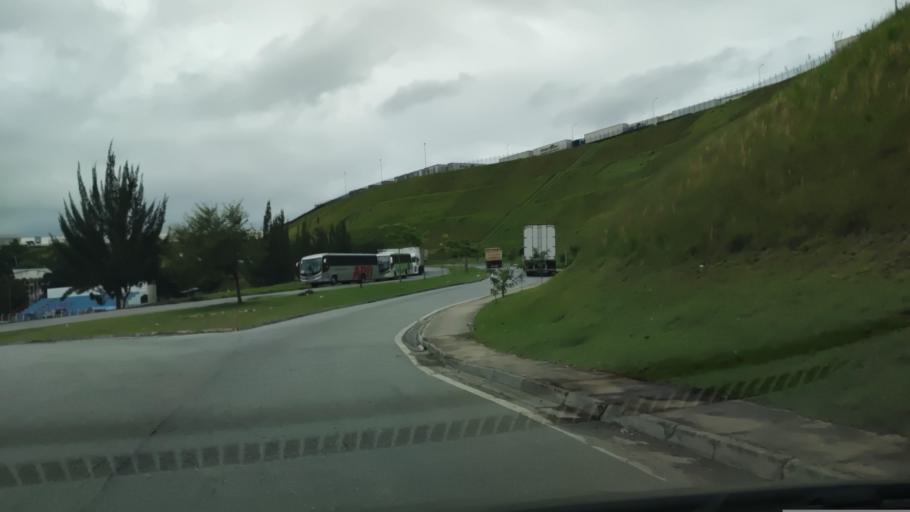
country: BR
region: Sao Paulo
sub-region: Cajamar
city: Cajamar
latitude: -23.3333
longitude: -46.8442
